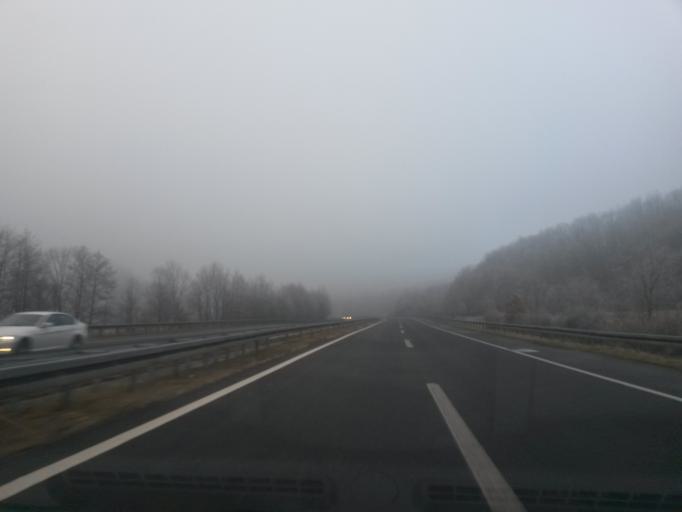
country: HR
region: Varazdinska
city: Remetinec
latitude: 46.1079
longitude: 16.2876
